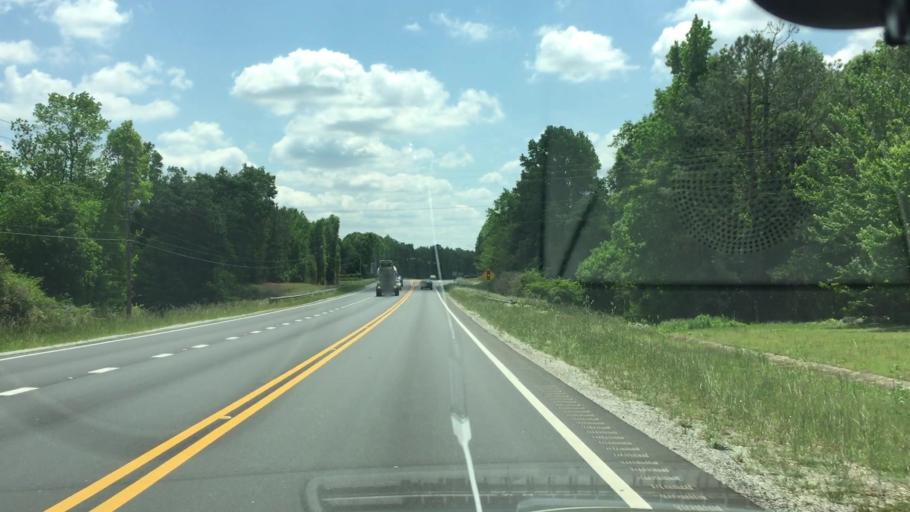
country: US
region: Alabama
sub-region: Lee County
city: Opelika
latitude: 32.6582
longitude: -85.3590
